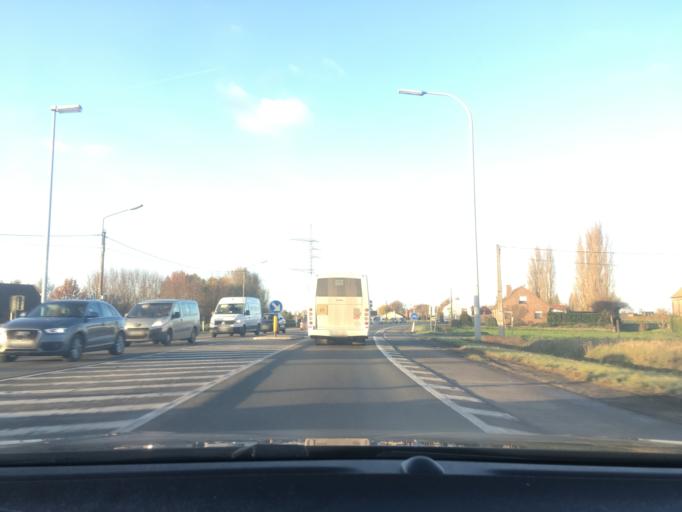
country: BE
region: Flanders
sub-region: Provincie West-Vlaanderen
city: Menen
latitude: 50.8204
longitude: 3.1191
